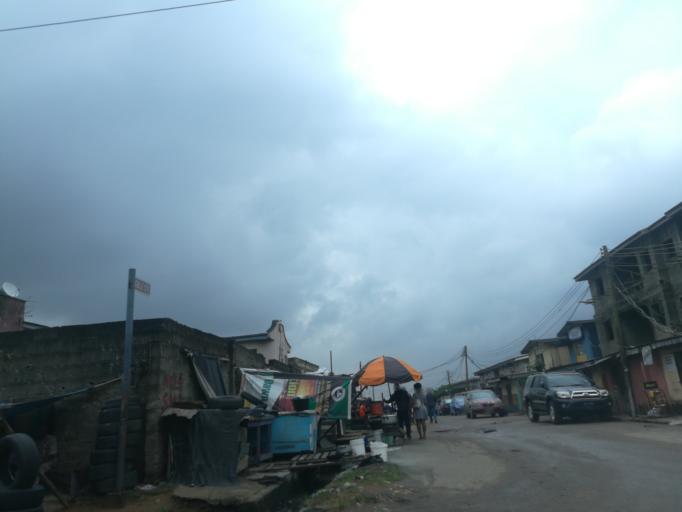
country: NG
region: Lagos
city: Ojota
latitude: 6.5693
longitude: 3.3744
